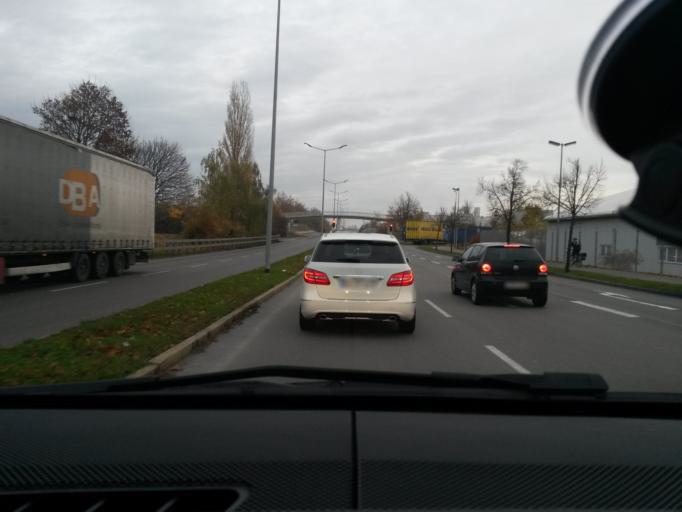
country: DE
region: Baden-Wuerttemberg
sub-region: Regierungsbezirk Stuttgart
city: Boeblingen
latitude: 48.6953
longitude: 8.9803
